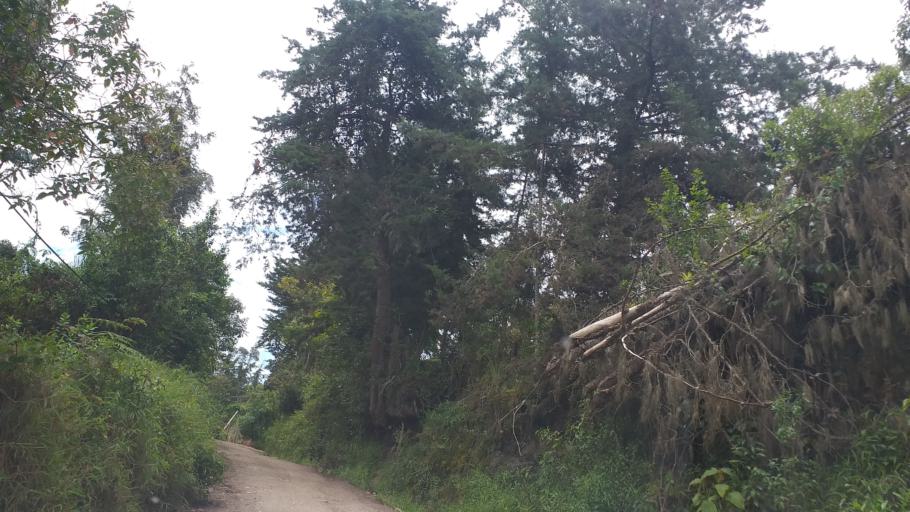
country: CO
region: Cundinamarca
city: Tenza
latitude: 5.0762
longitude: -73.4579
